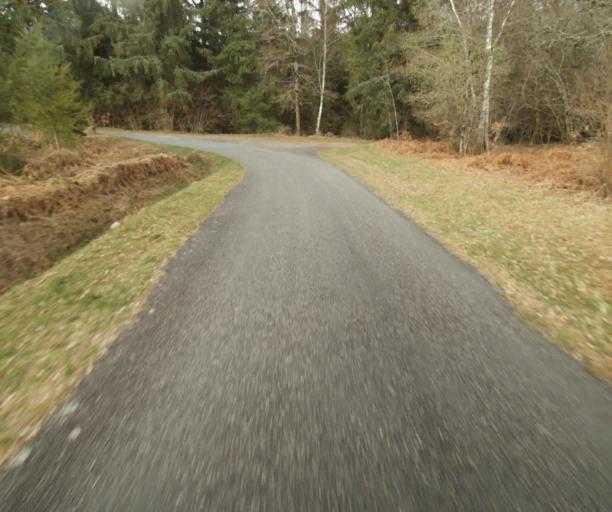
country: FR
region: Limousin
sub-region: Departement de la Correze
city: Egletons
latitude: 45.2723
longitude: 1.9980
